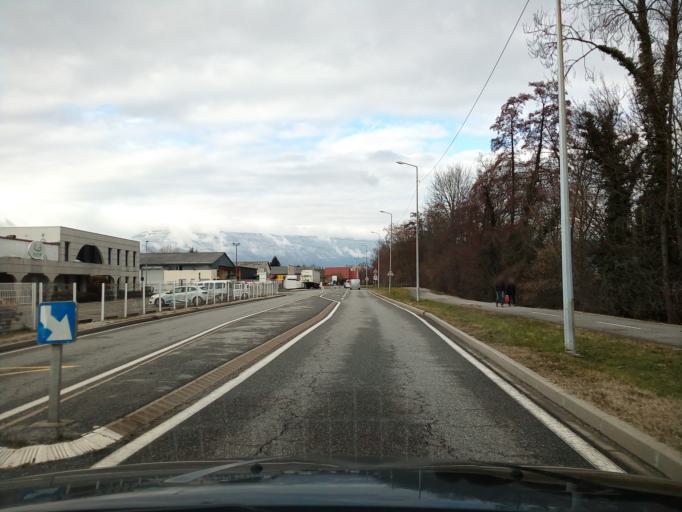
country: FR
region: Rhone-Alpes
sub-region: Departement de la Savoie
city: Barberaz
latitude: 45.5561
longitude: 5.9505
